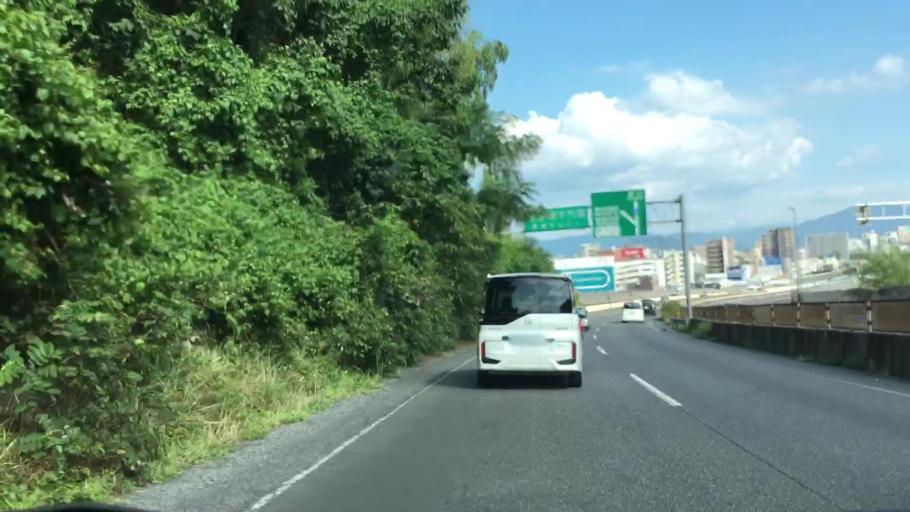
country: JP
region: Hiroshima
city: Hiroshima-shi
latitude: 34.3945
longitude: 132.4191
